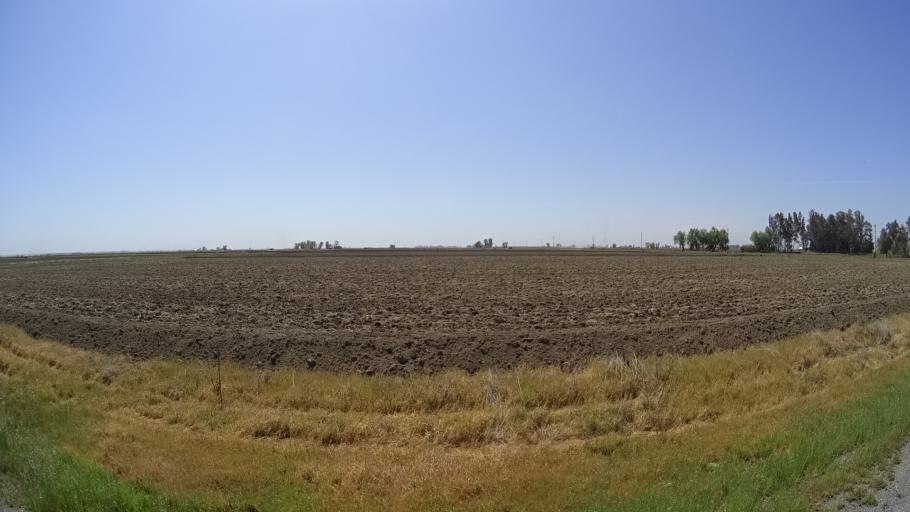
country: US
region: California
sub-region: Glenn County
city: Willows
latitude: 39.5437
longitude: -122.0966
